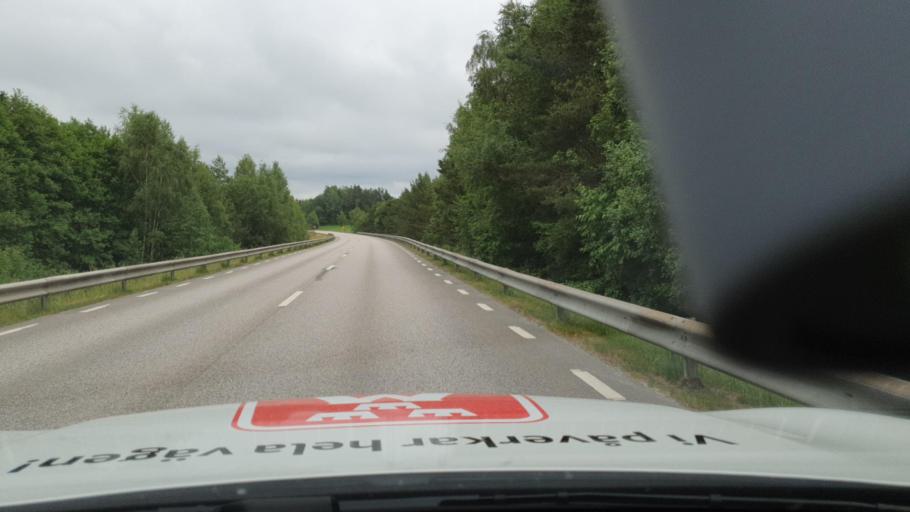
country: SE
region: Vaestra Goetaland
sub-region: Tibro Kommun
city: Tibro
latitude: 58.3591
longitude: 14.2152
